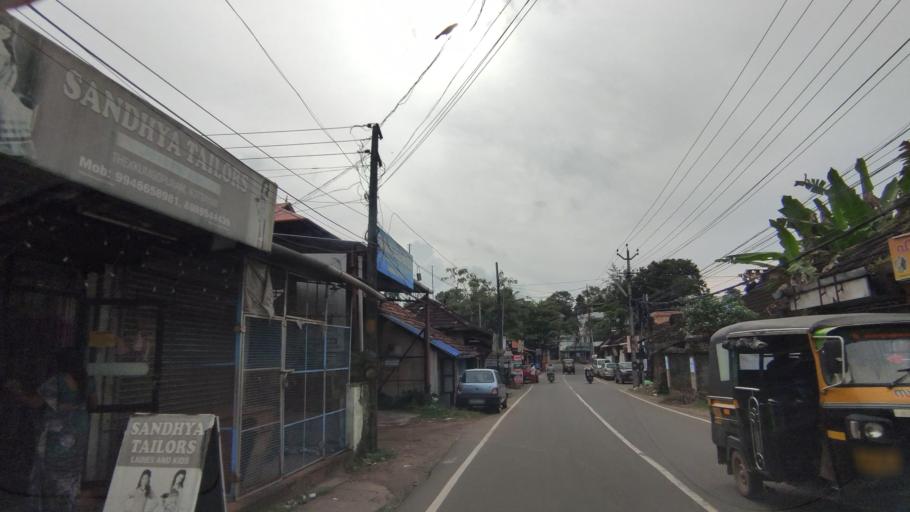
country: IN
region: Kerala
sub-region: Kottayam
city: Kottayam
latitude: 9.5877
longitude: 76.5187
